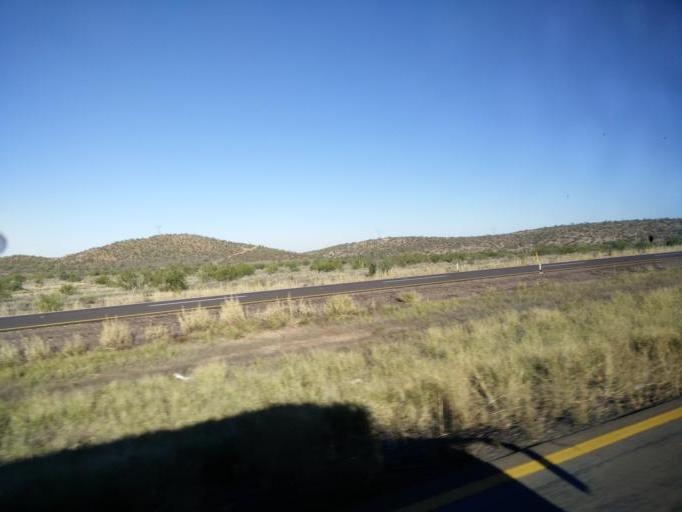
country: MX
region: Sonora
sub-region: Empalme
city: La Palma
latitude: 28.4783
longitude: -111.0458
